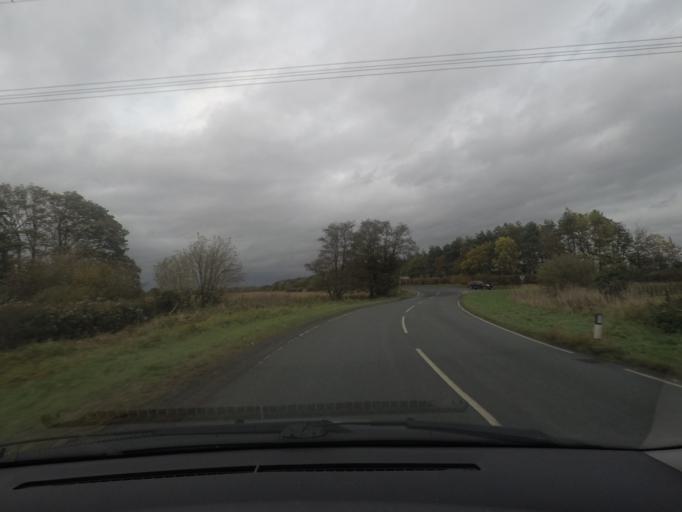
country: GB
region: England
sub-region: City of York
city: Wigginton
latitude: 54.0878
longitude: -1.1107
